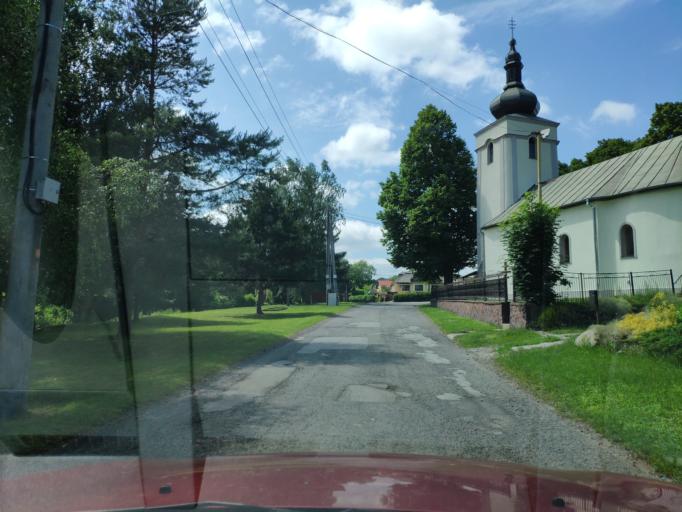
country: SK
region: Presovsky
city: Vranov nad Topl'ou
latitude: 48.8039
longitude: 21.6424
